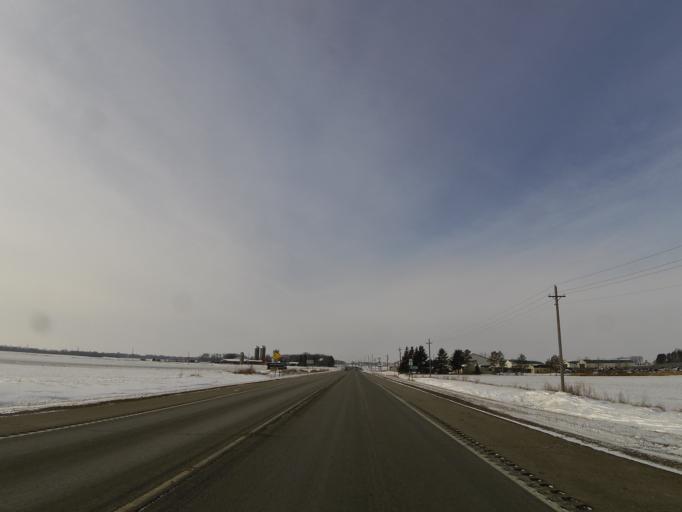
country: US
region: Minnesota
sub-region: McLeod County
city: Lester Prairie
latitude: 44.9063
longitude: -94.0260
